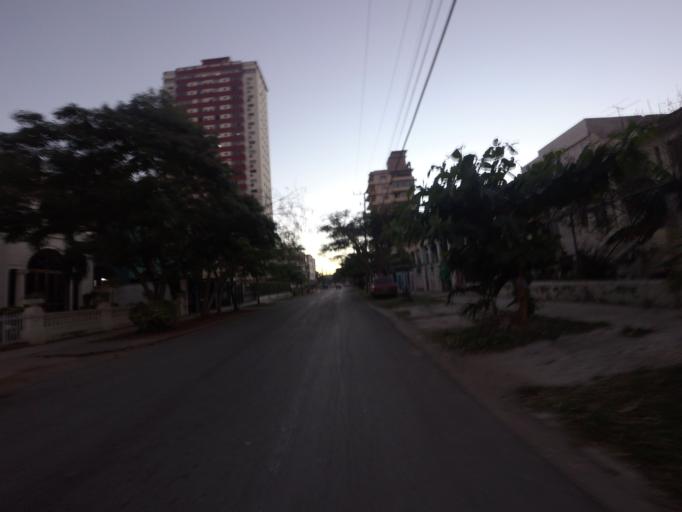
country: CU
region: La Habana
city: Havana
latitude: 23.1431
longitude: -82.3901
